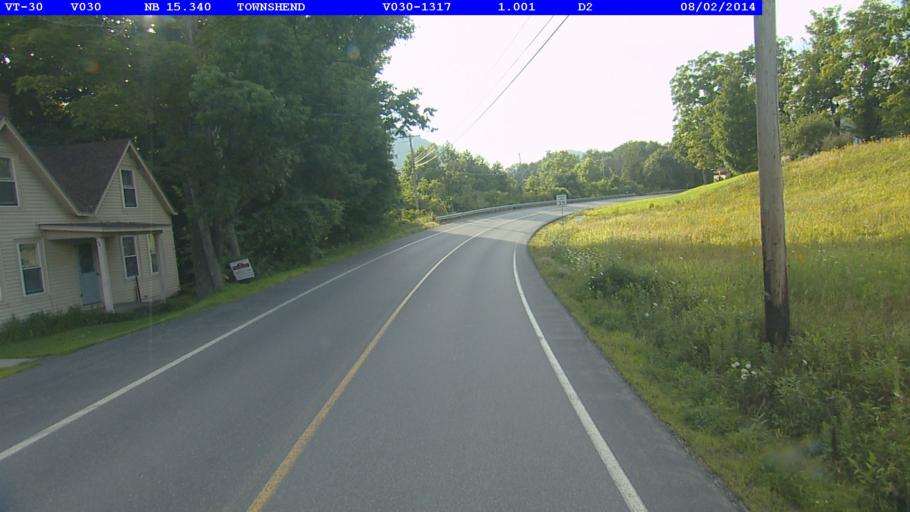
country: US
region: Vermont
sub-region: Windham County
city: Newfane
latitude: 43.0322
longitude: -72.6628
